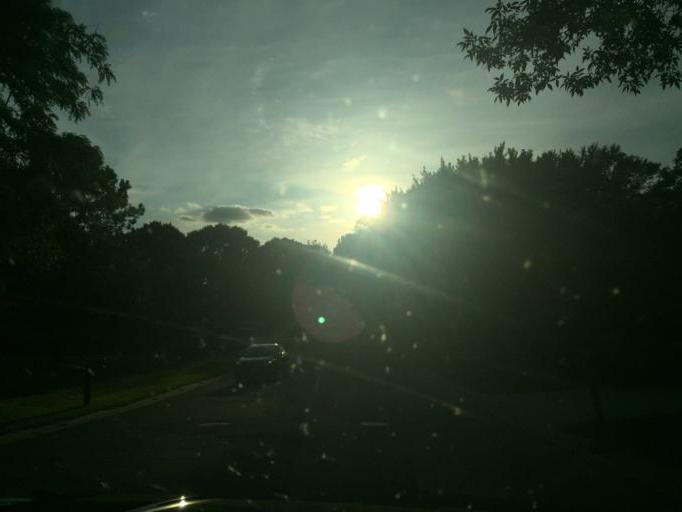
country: US
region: Minnesota
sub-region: Olmsted County
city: Rochester
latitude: 44.0168
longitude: -92.4925
